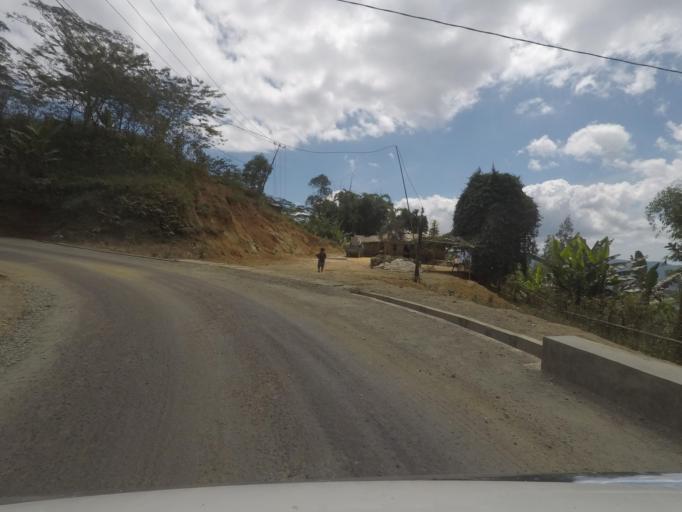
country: TL
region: Ermera
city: Gleno
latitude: -8.7485
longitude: 125.3527
